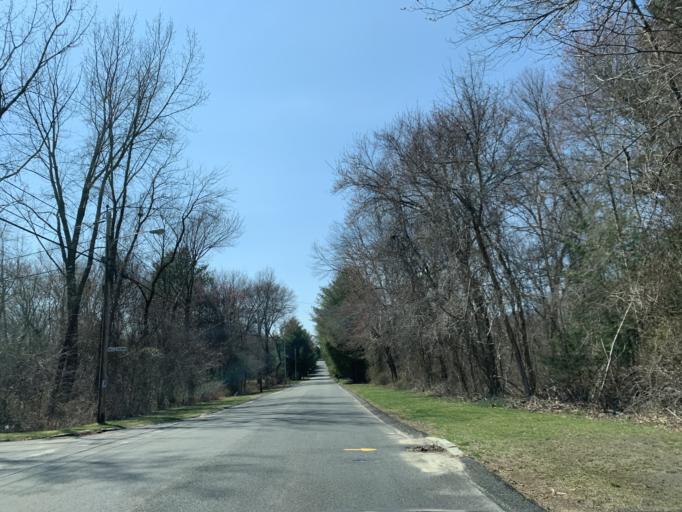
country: US
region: Rhode Island
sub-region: Kent County
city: East Greenwich
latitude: 41.6330
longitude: -71.4291
